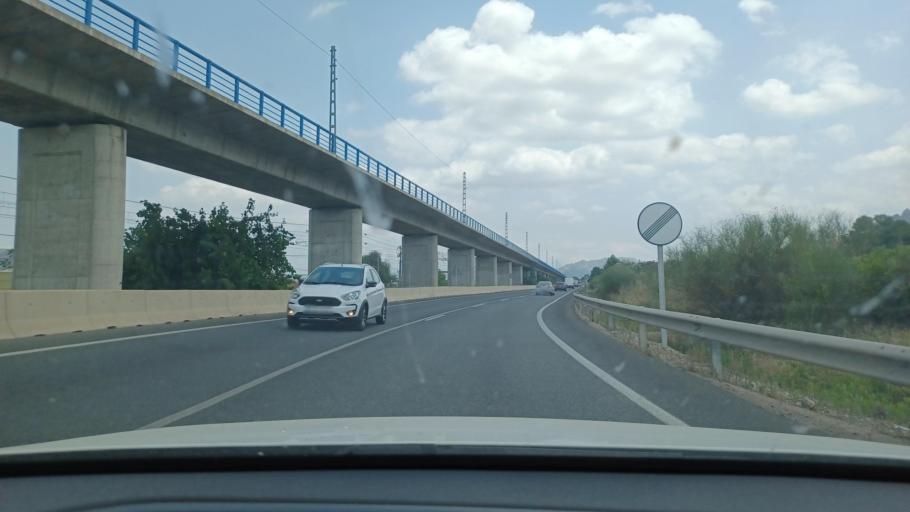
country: ES
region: Valencia
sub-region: Provincia de Valencia
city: Valles
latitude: 38.9809
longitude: -0.5511
